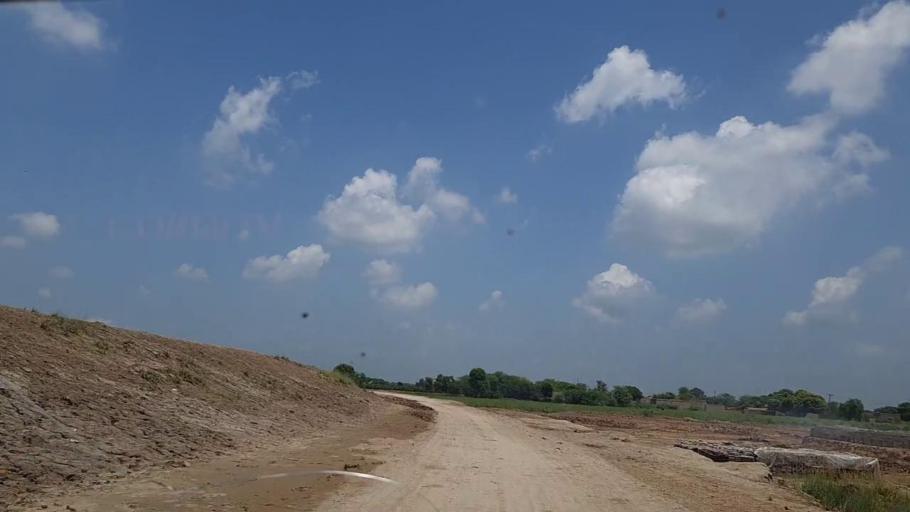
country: PK
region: Sindh
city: Tharu Shah
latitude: 26.9878
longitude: 68.0600
